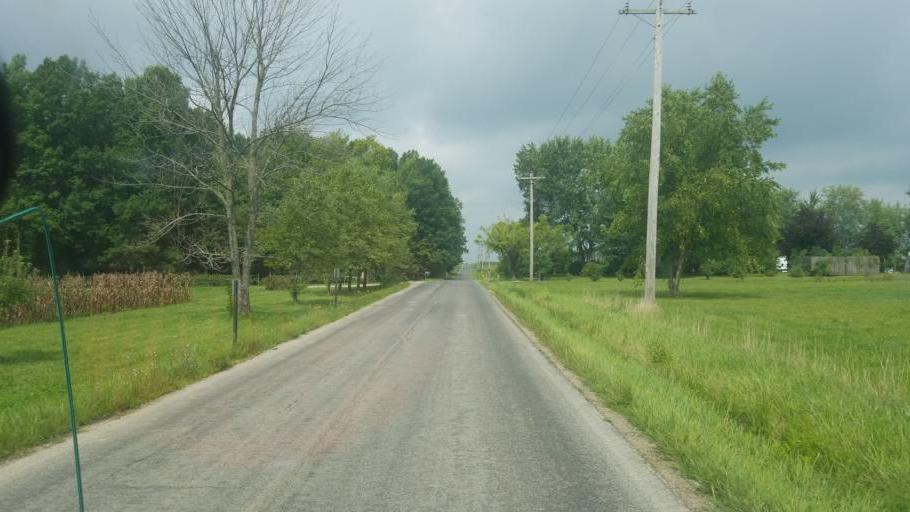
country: US
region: Ohio
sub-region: Huron County
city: Greenwich
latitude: 40.9895
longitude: -82.4779
